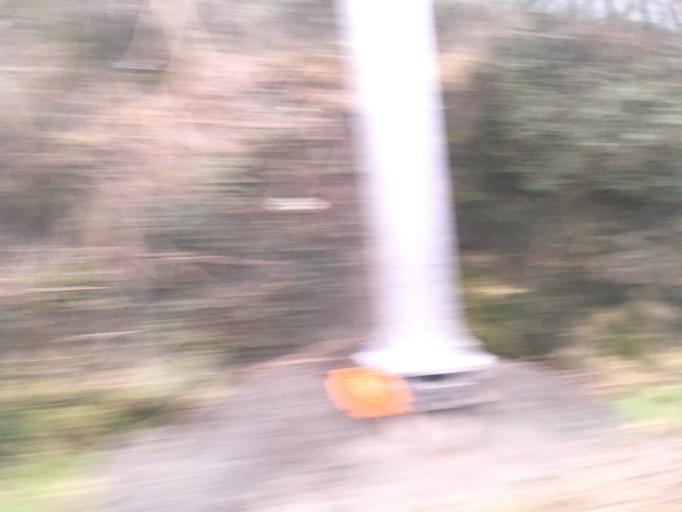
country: GB
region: England
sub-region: South Gloucestershire
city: Winterbourne
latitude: 51.5168
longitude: -2.5047
